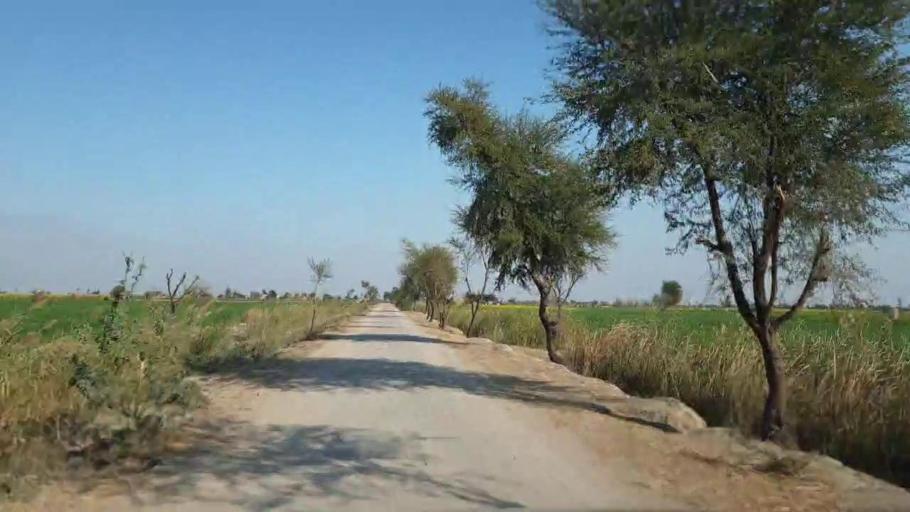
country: PK
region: Sindh
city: Khadro
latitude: 26.1644
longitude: 68.7587
